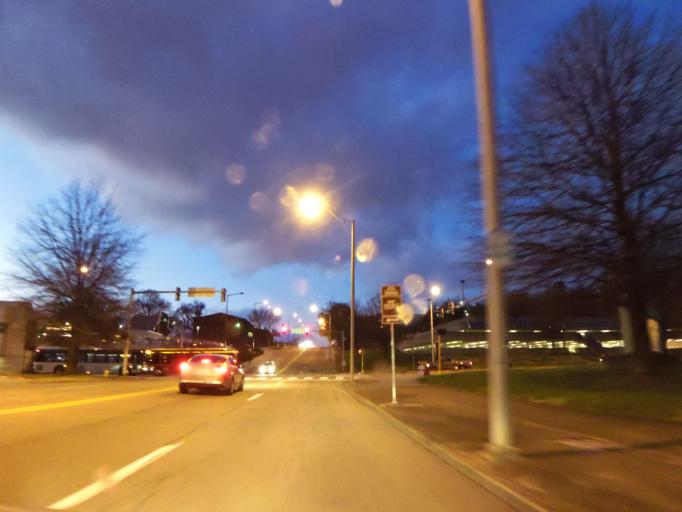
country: US
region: Tennessee
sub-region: Knox County
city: Knoxville
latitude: 35.9651
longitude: -83.9125
